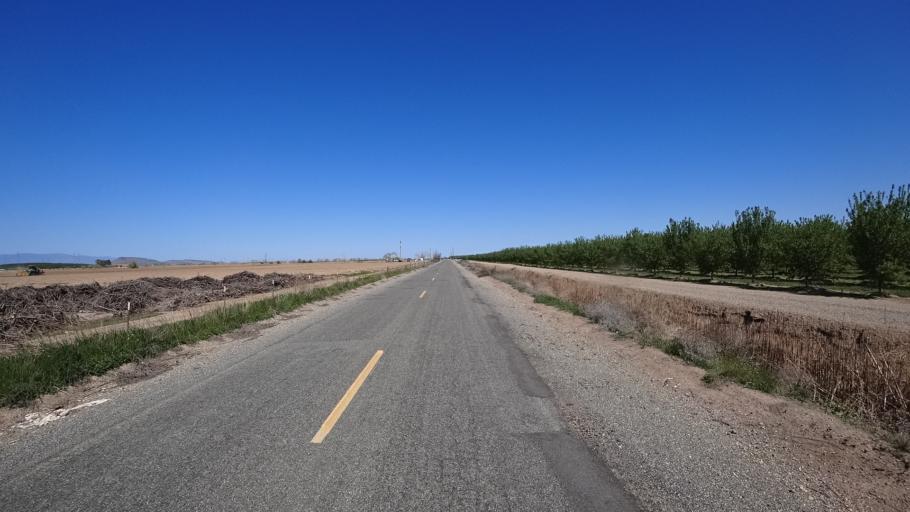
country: US
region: California
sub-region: Glenn County
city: Orland
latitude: 39.6908
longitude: -122.2530
